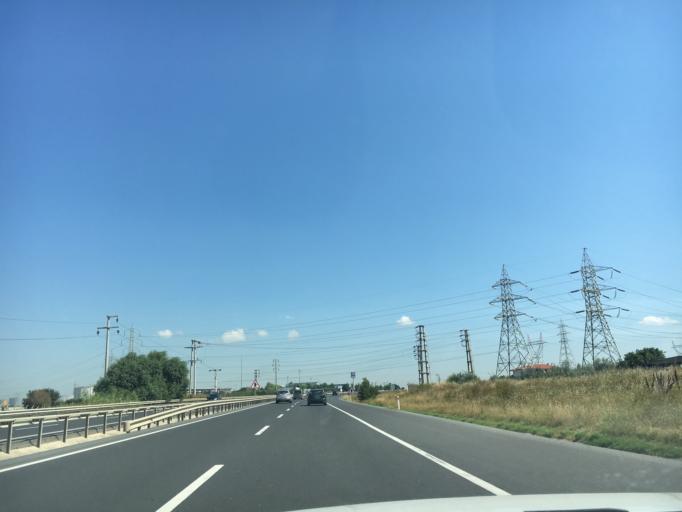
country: TR
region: Tekirdag
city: Marmara Ereglisi
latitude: 40.9928
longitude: 27.9727
